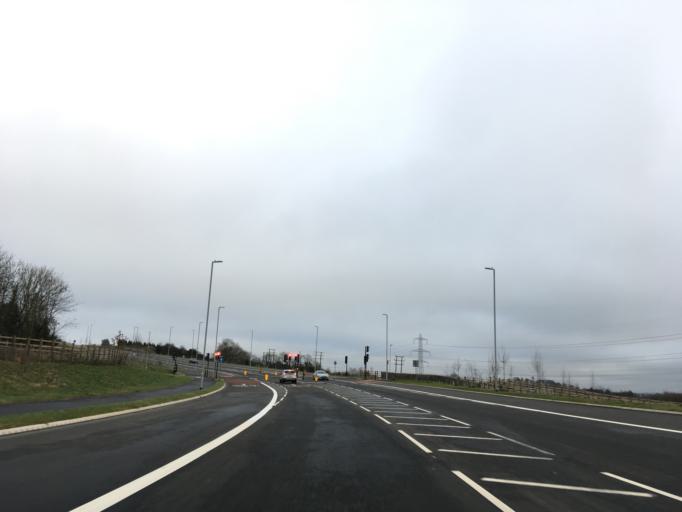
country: GB
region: England
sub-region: South Gloucestershire
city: Stoke Gifford
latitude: 51.5112
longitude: -2.5311
